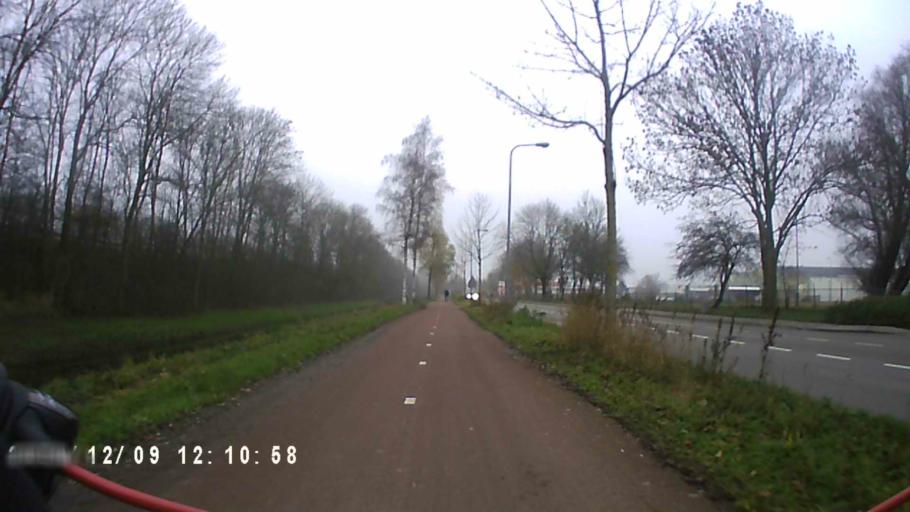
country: NL
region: Groningen
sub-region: Gemeente Groningen
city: Oosterpark
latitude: 53.2046
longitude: 6.6006
